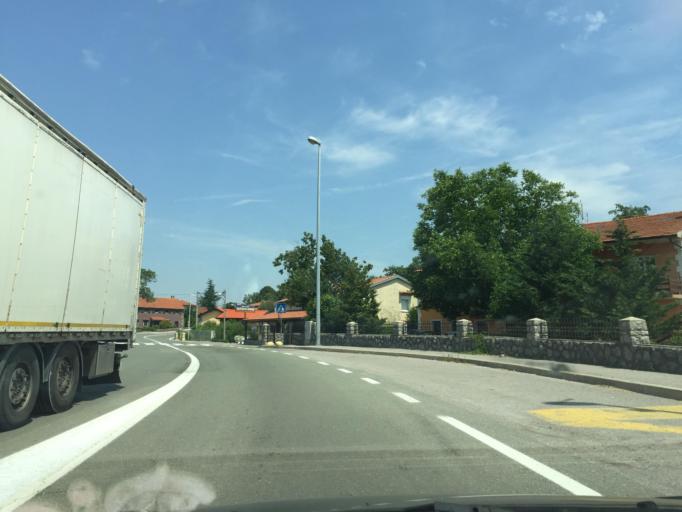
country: HR
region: Primorsko-Goranska
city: Matulji
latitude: 45.3993
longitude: 14.3084
